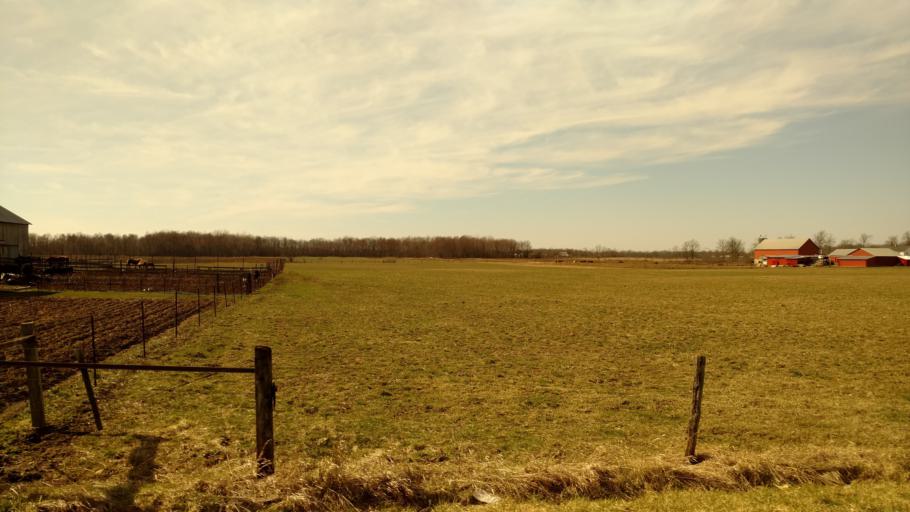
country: US
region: Ohio
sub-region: Hardin County
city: Kenton
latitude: 40.5977
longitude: -83.5041
